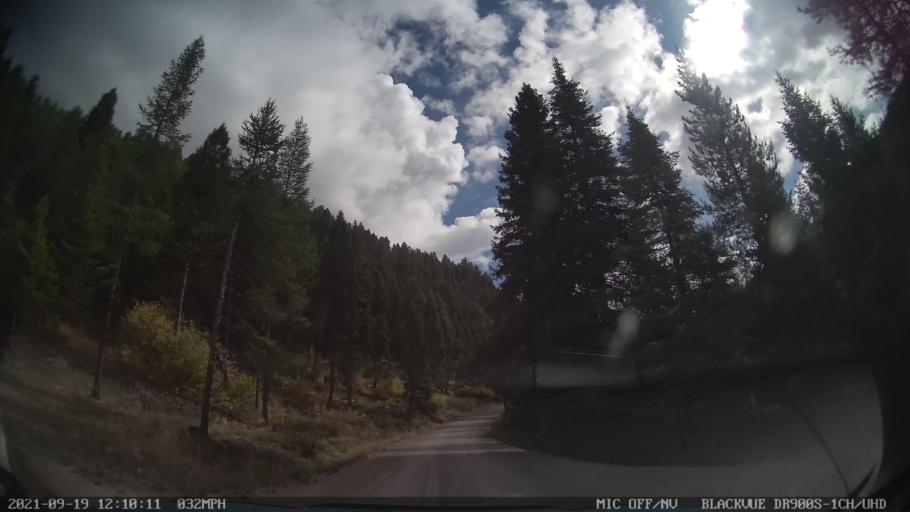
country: US
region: Montana
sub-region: Missoula County
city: Seeley Lake
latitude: 47.1801
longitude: -113.3858
